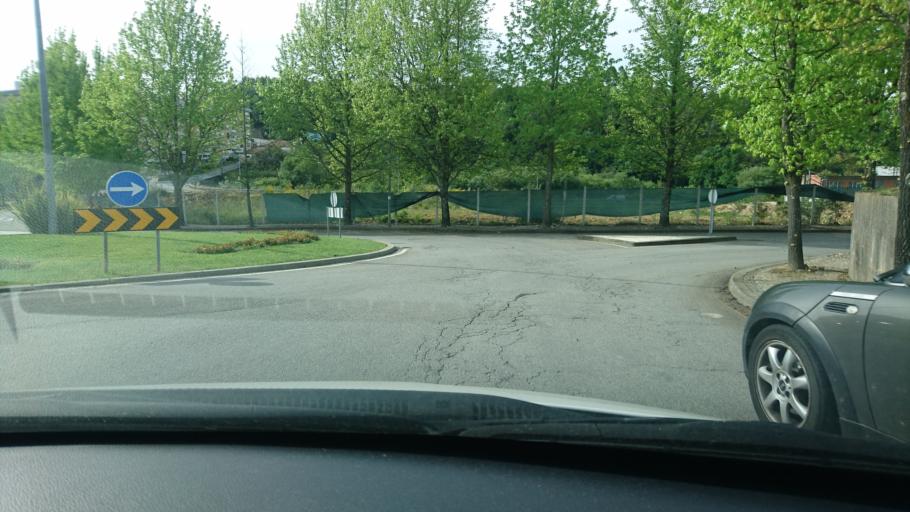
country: PT
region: Aveiro
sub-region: Oliveira de Azemeis
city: Oliveira de Azemeis
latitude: 40.8466
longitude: -8.4791
